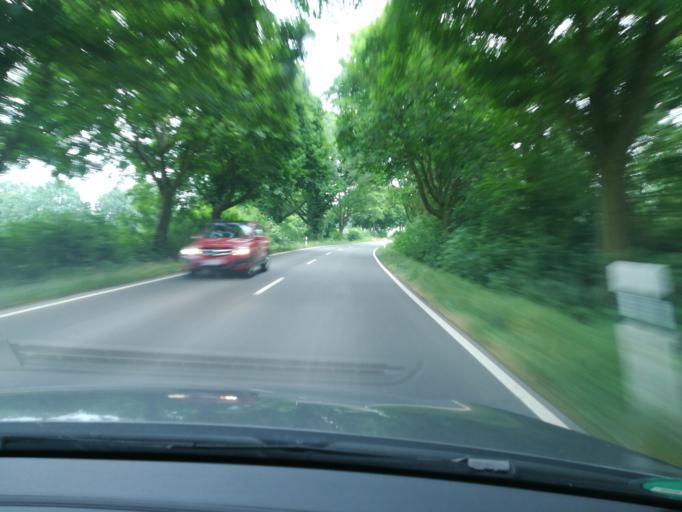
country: DE
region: Schleswig-Holstein
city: Siek
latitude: 53.6322
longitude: 10.3141
